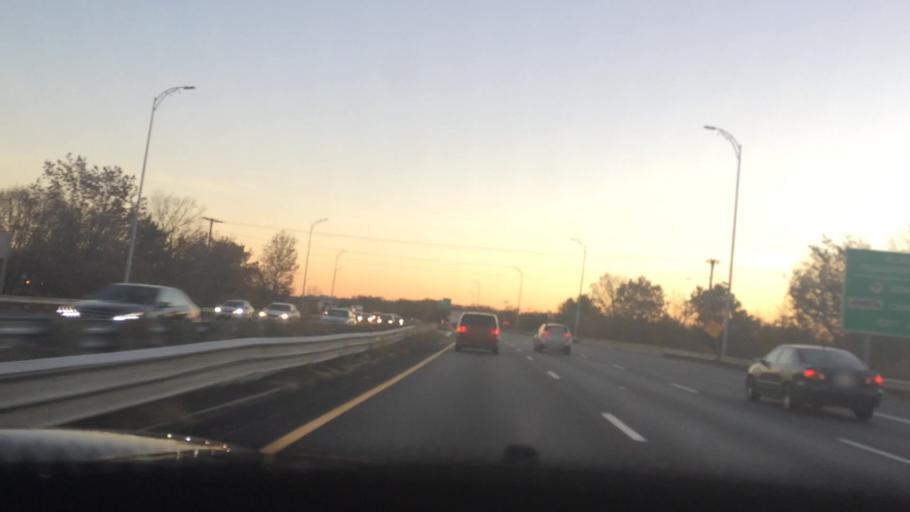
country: US
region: Massachusetts
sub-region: Essex County
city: North Andover
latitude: 42.6985
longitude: -71.1418
